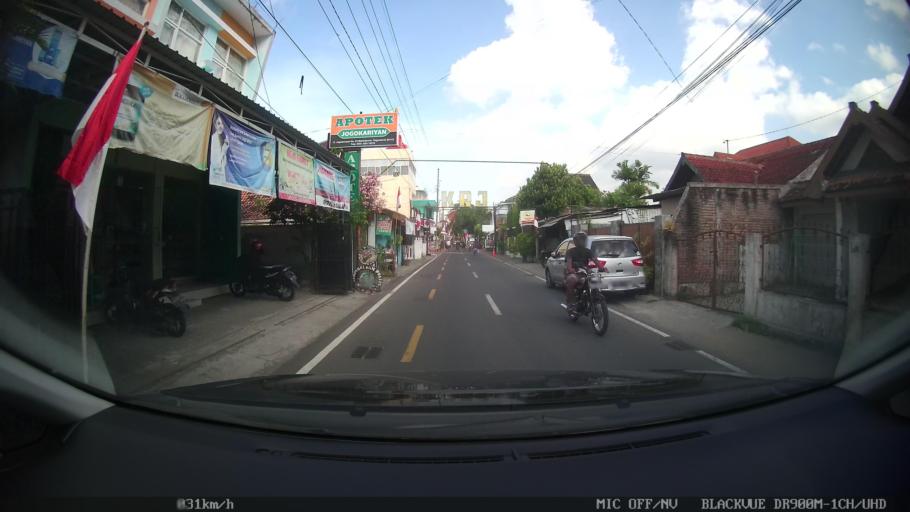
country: ID
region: Daerah Istimewa Yogyakarta
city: Kasihan
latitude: -7.8242
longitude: 110.3652
